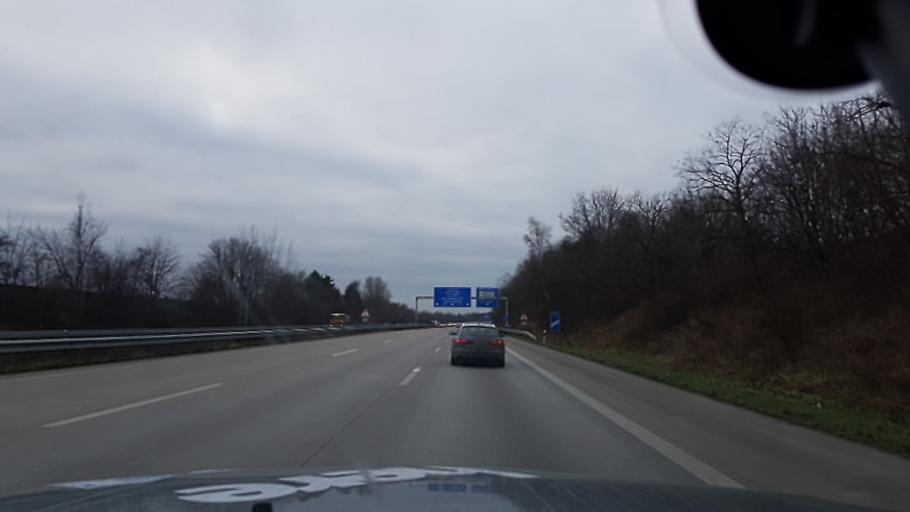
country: DE
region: Schleswig-Holstein
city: Stockelsdorf
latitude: 53.8883
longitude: 10.6679
